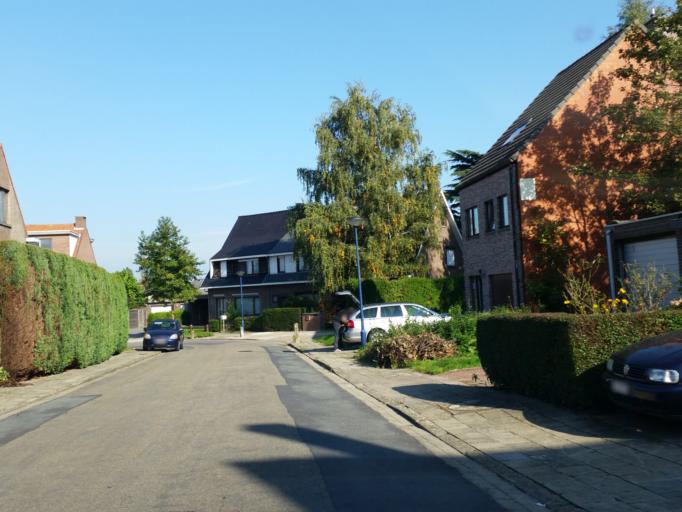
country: BE
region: Flanders
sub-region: Provincie Antwerpen
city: Kontich
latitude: 51.1316
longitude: 4.4541
